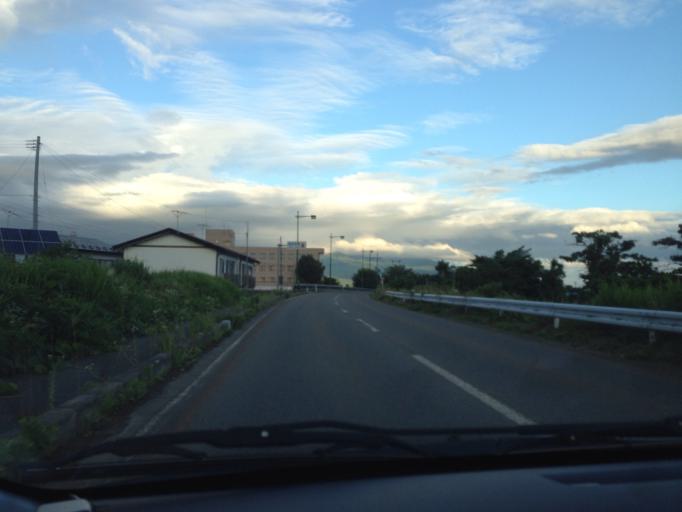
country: JP
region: Fukushima
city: Kitakata
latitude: 37.6820
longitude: 139.8660
